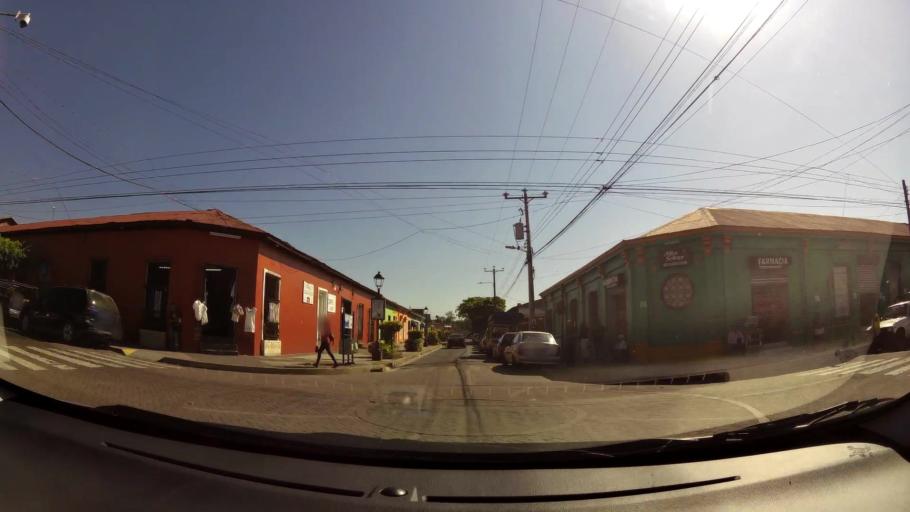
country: SV
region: La Libertad
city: Santa Tecla
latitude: 13.6754
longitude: -89.2880
